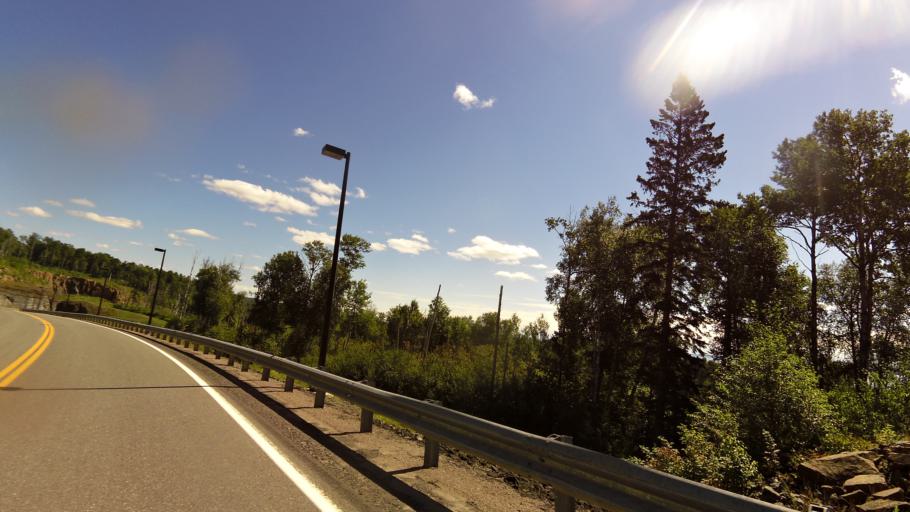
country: CA
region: Ontario
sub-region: Thunder Bay District
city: Thunder Bay
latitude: 48.4866
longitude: -89.1631
